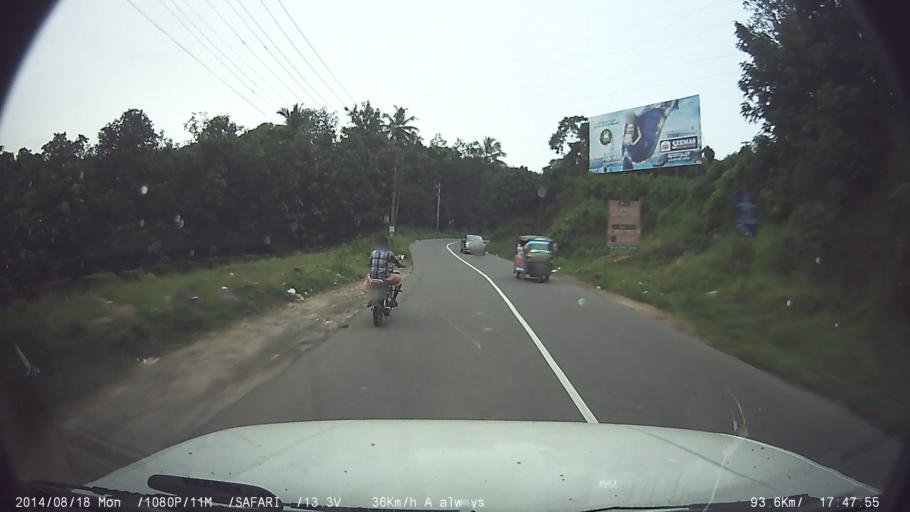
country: IN
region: Kerala
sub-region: Ernakulam
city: Muvattupuzha
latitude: 9.9623
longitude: 76.5773
